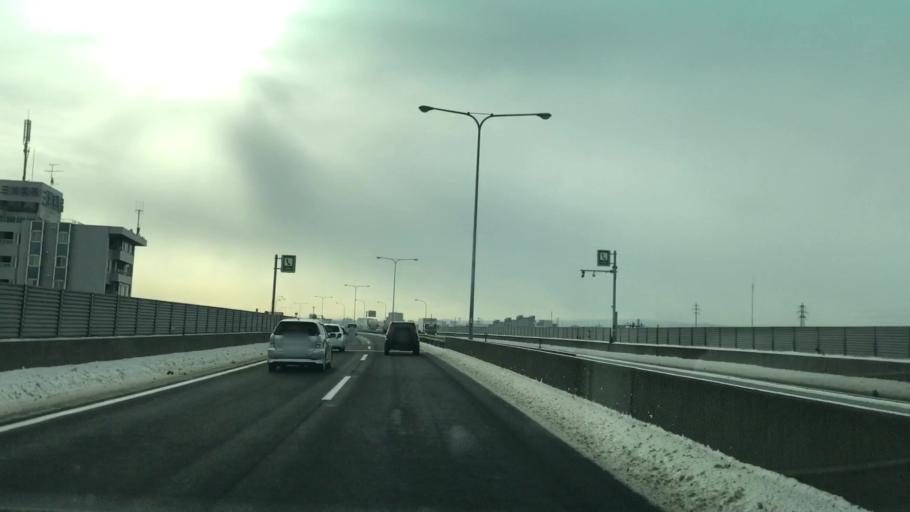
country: JP
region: Hokkaido
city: Sapporo
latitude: 43.0605
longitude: 141.4248
